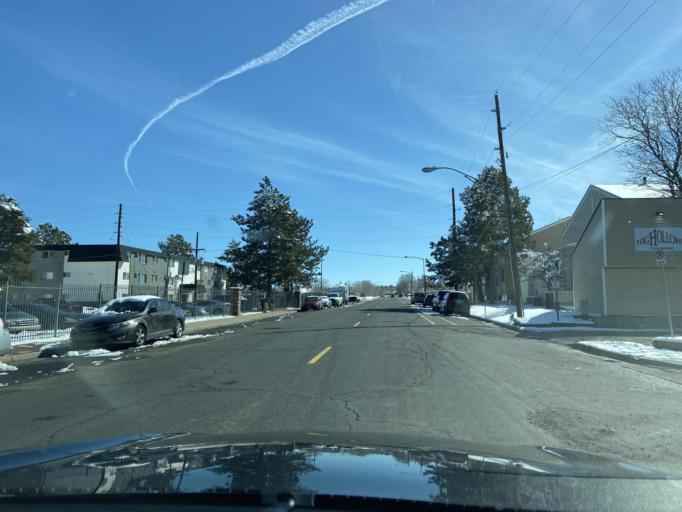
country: US
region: Colorado
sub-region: Adams County
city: Aurora
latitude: 39.7038
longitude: -104.8637
